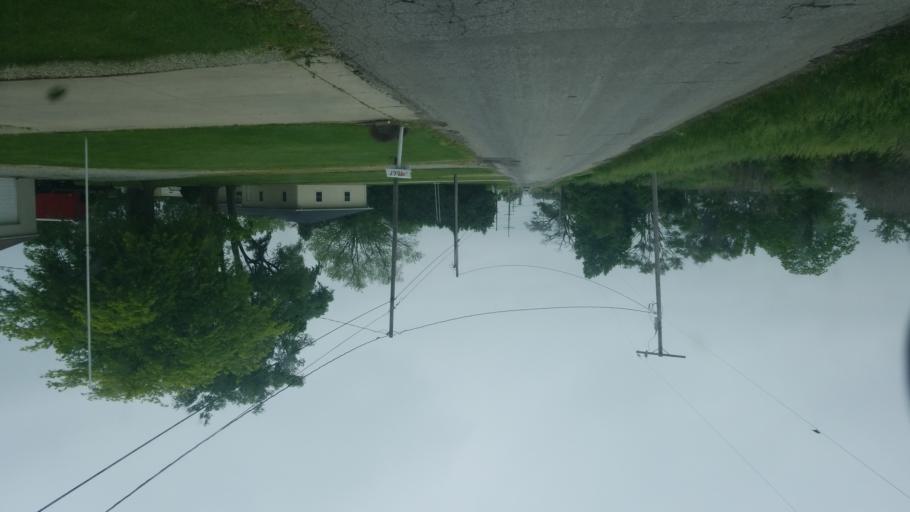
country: US
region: Indiana
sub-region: Marshall County
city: Bremen
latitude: 41.4555
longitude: -86.1177
